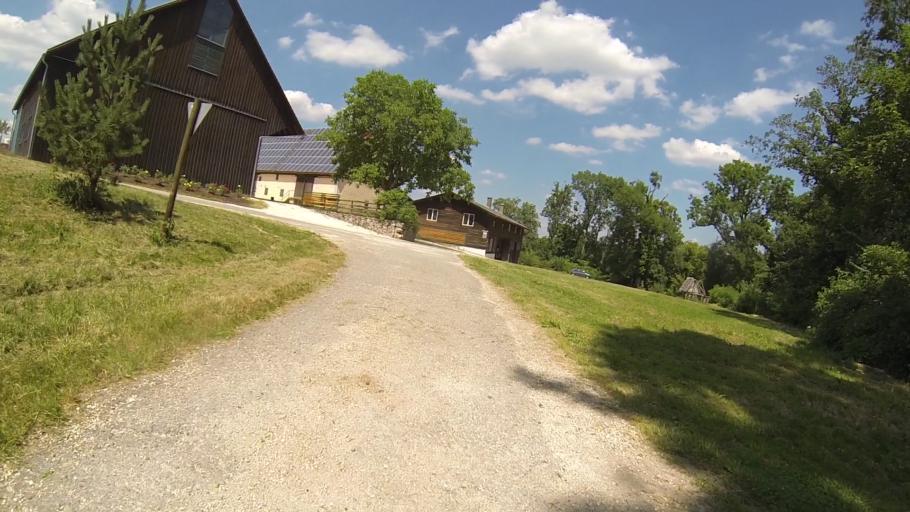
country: DE
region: Baden-Wuerttemberg
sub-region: Regierungsbezirk Stuttgart
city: Herbrechtingen
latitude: 48.5999
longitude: 10.1634
